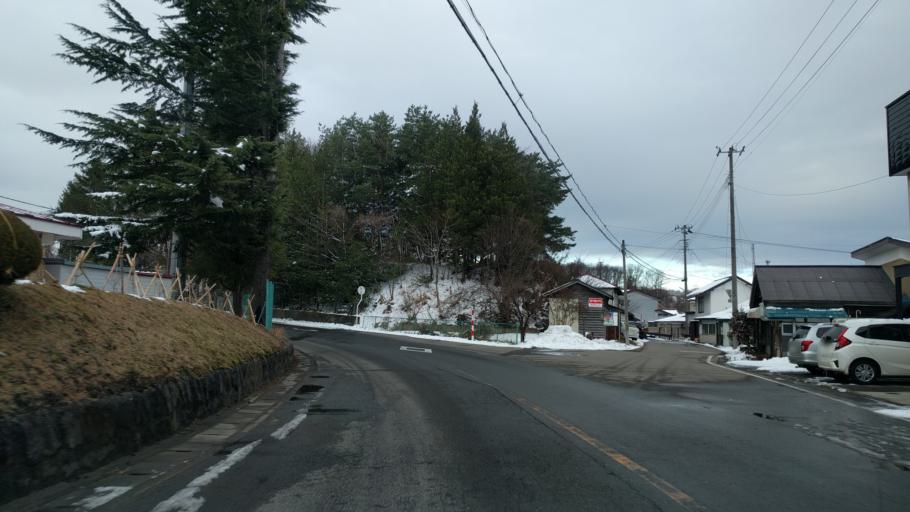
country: JP
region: Fukushima
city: Kitakata
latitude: 37.5640
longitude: 139.9487
